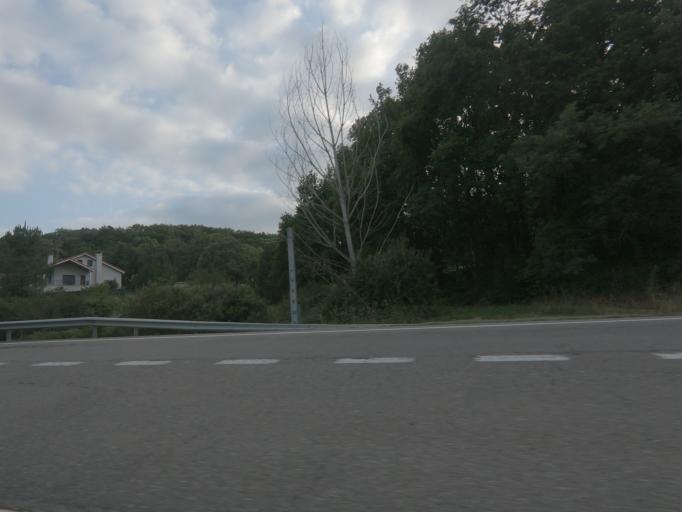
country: ES
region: Galicia
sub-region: Provincia de Ourense
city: Taboadela
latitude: 42.2370
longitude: -7.8460
